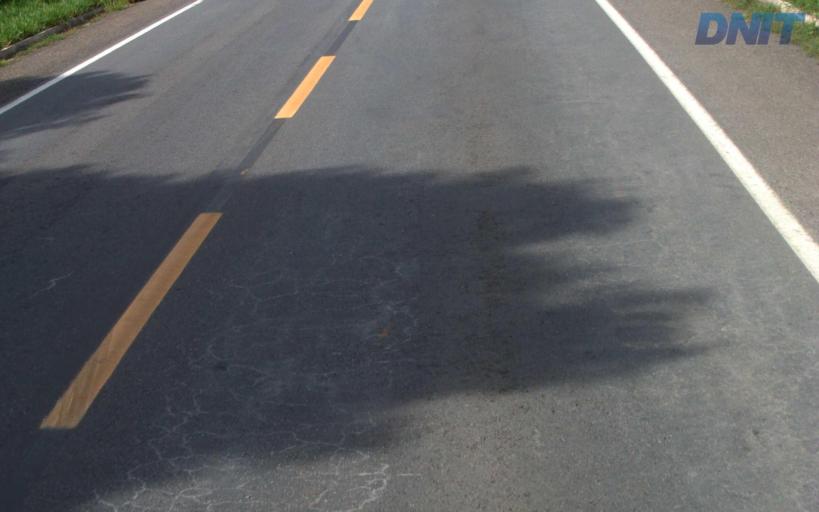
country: BR
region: Minas Gerais
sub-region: Belo Oriente
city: Belo Oriente
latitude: -19.1794
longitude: -42.2589
